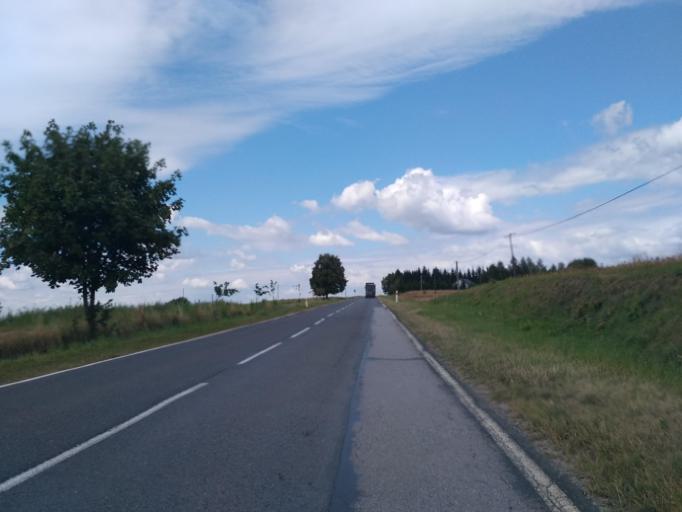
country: PL
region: Subcarpathian Voivodeship
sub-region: Powiat przeworski
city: Jawornik Polski
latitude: 49.8906
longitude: 22.2371
